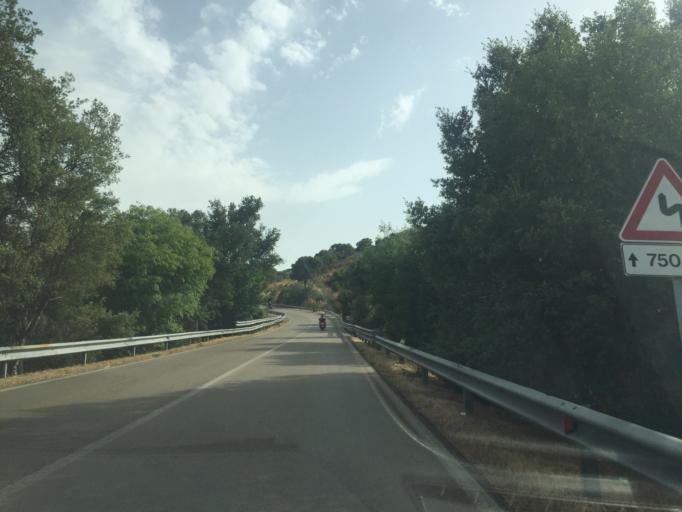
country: IT
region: Sardinia
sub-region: Provincia di Olbia-Tempio
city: Luras
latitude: 40.9582
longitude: 9.2067
